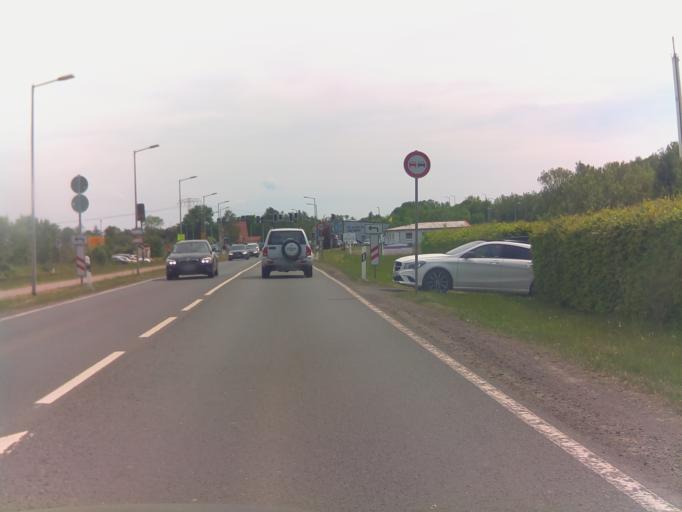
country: DE
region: Thuringia
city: Niedersachswerfen
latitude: 51.5407
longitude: 10.7689
